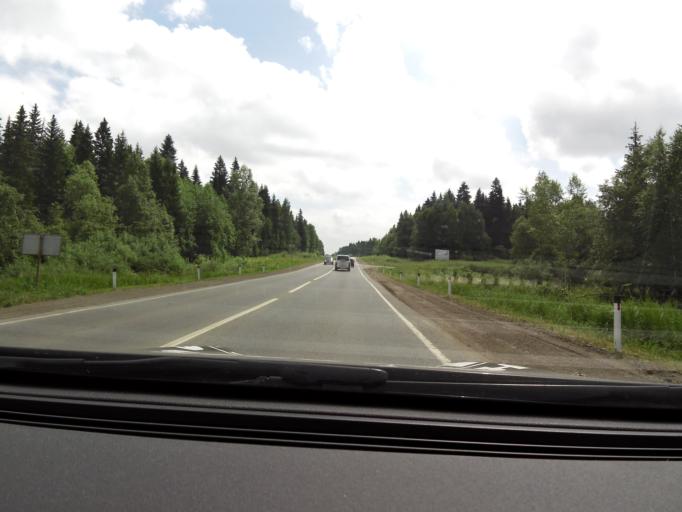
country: RU
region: Perm
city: Bershet'
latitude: 57.6988
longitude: 56.3888
